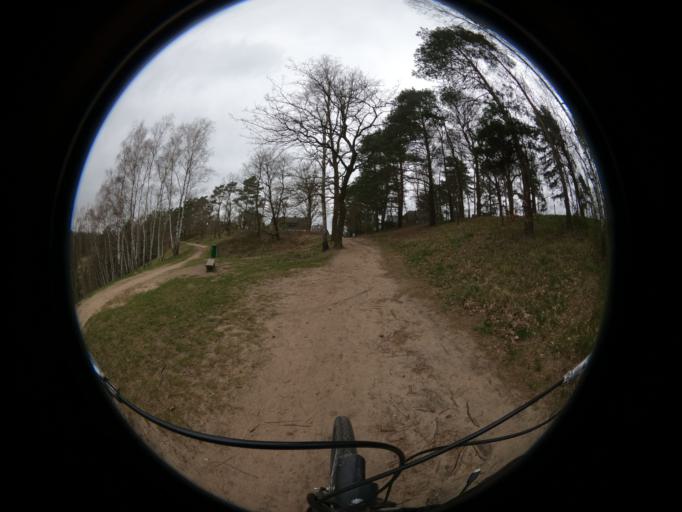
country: DE
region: Lower Saxony
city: Neu Wulmstorf
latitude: 53.4641
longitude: 9.8455
